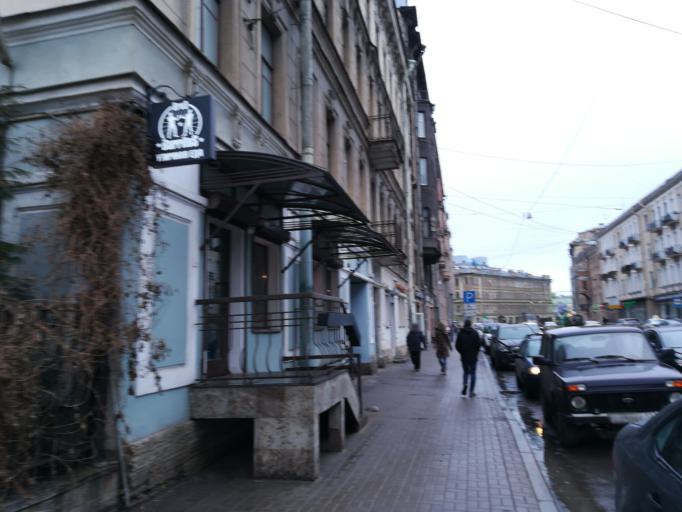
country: RU
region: St.-Petersburg
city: Petrogradka
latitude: 59.9568
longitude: 30.3313
